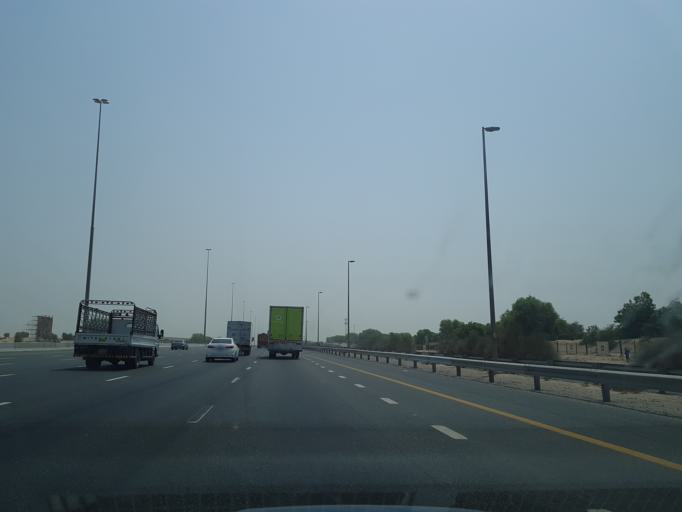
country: AE
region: Dubai
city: Dubai
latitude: 25.0593
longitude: 55.2688
